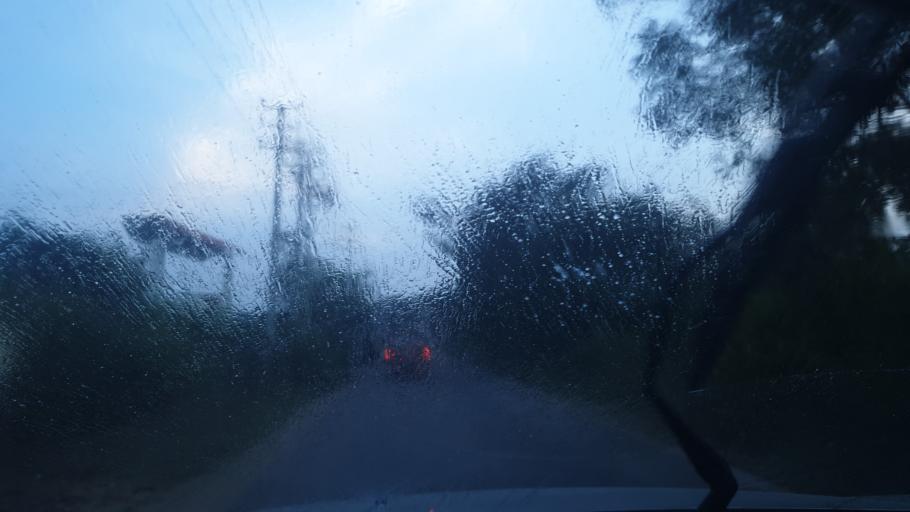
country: IN
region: Karnataka
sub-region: Bangalore Rural
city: Hoskote
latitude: 13.0776
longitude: 77.7041
